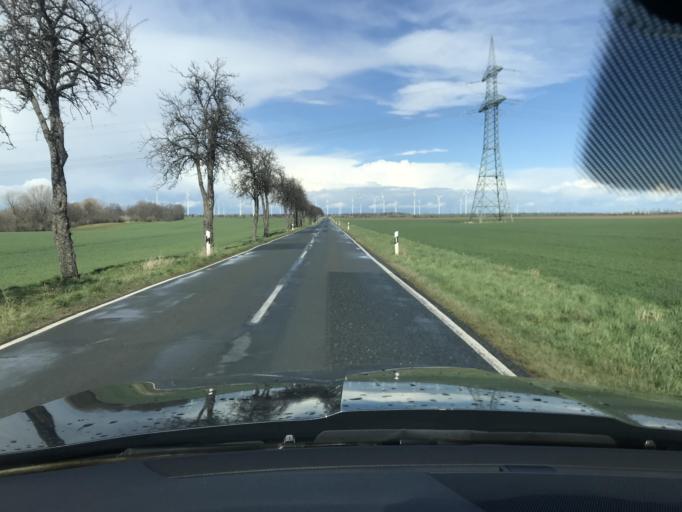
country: DE
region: Saxony-Anhalt
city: Frose
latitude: 51.7358
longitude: 11.3573
